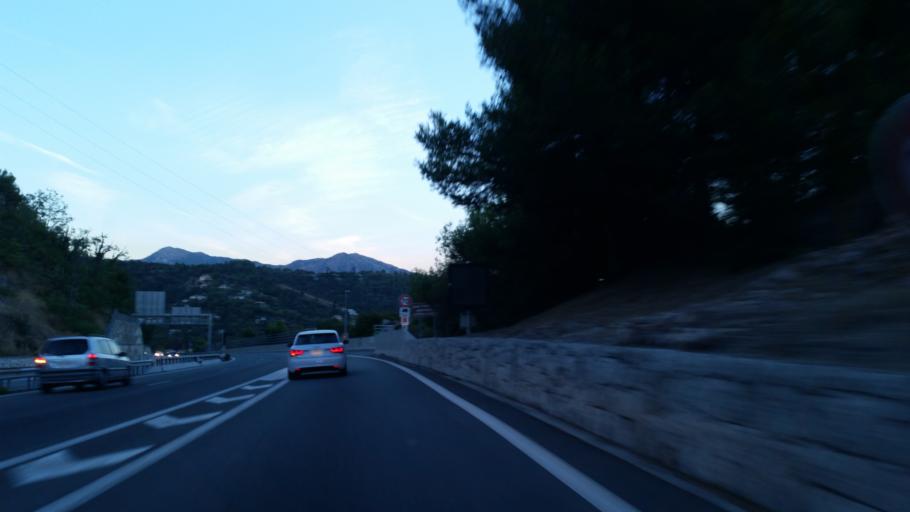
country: MC
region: Commune de Monaco
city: Saint-Roman
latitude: 43.7607
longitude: 7.4462
